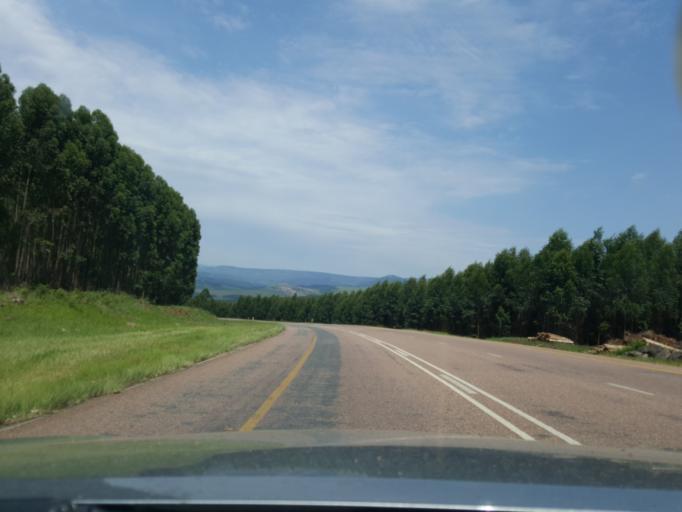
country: ZA
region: Mpumalanga
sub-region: Ehlanzeni District
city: White River
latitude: -25.1944
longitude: 31.0287
